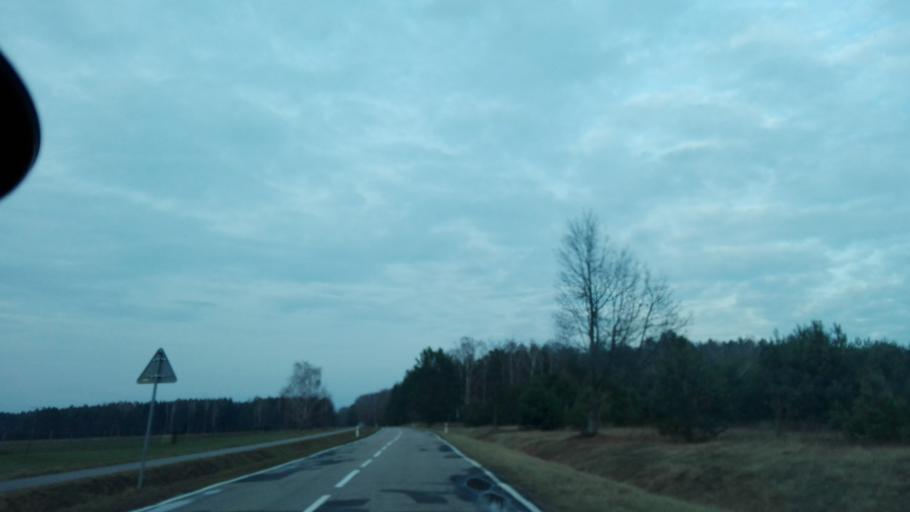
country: PL
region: Lublin Voivodeship
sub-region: Powiat bialski
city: Slawatycze
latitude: 51.6998
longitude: 23.5012
